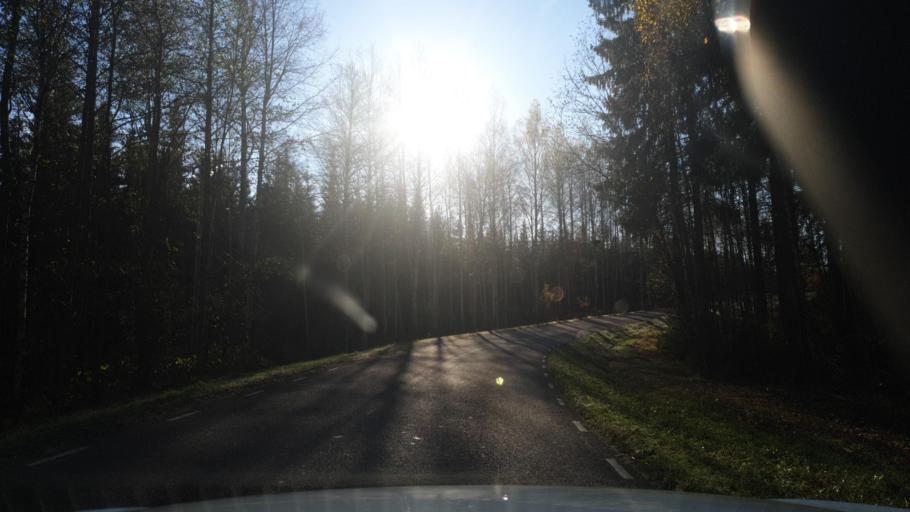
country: SE
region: Vaermland
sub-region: Karlstads Kommun
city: Valberg
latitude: 59.4511
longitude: 13.0931
